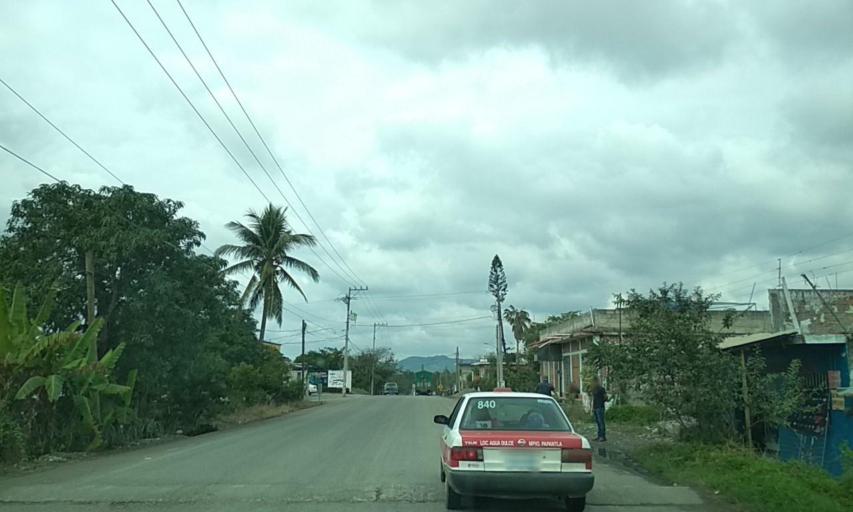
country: MX
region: Veracruz
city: Agua Dulce
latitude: 20.3638
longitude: -97.3314
